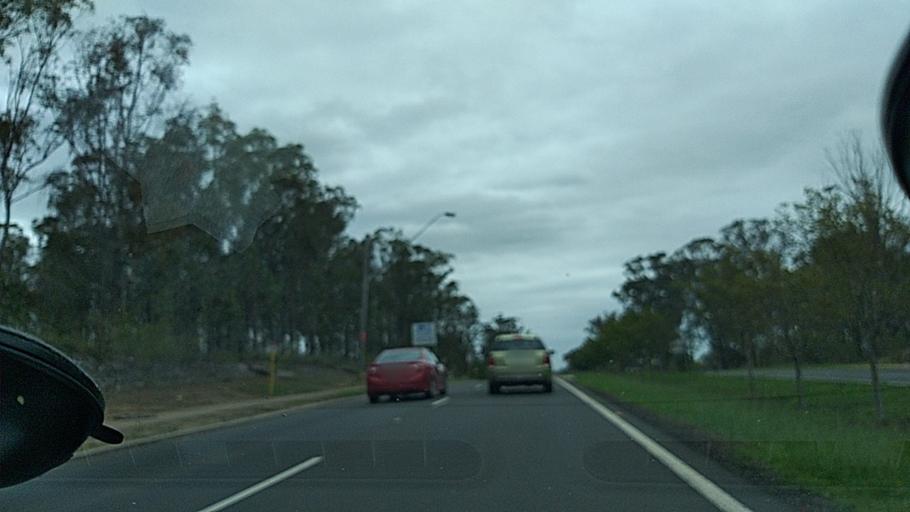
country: AU
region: New South Wales
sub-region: Penrith Municipality
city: Cambridge Park
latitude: -33.7500
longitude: 150.7140
